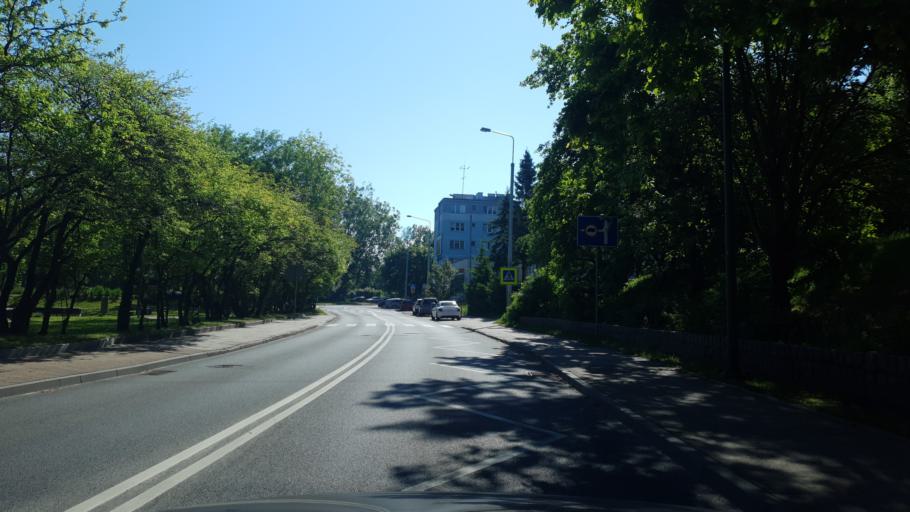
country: PL
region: Pomeranian Voivodeship
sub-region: Sopot
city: Sopot
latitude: 54.4556
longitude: 18.5512
